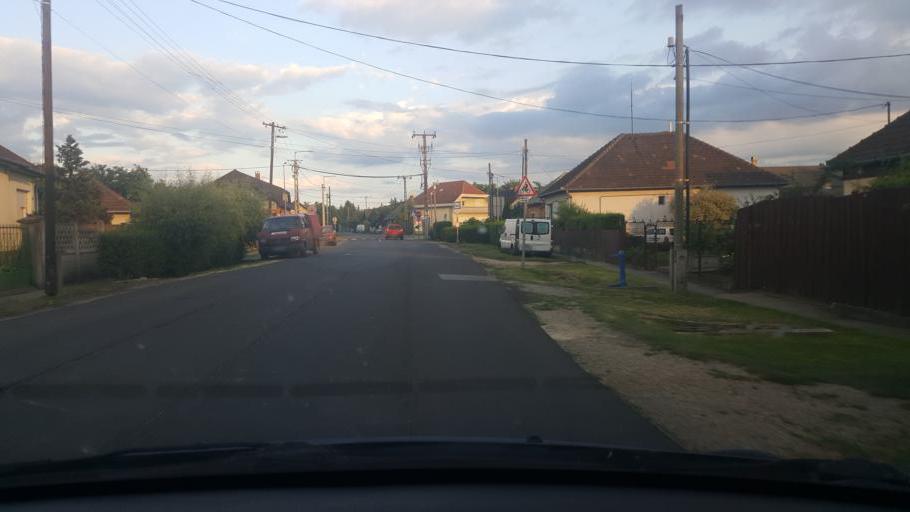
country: HU
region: Pest
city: Monor
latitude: 47.3418
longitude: 19.4417
